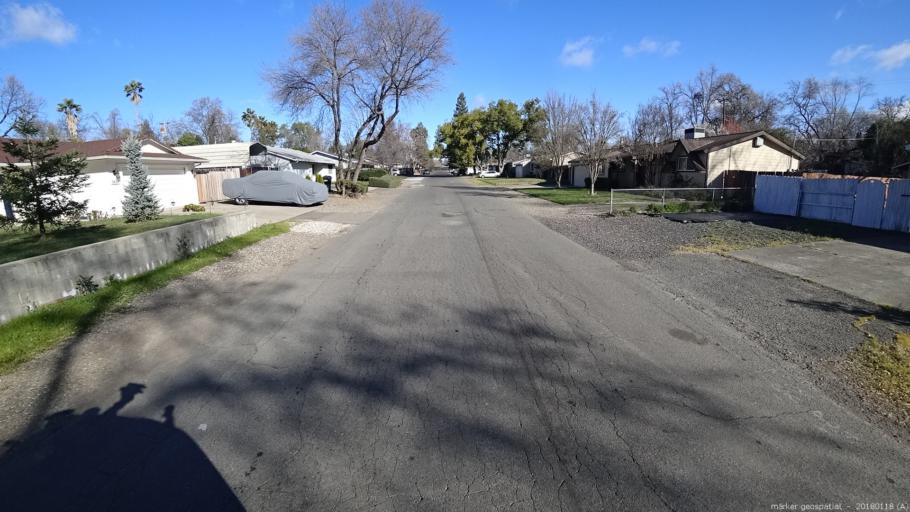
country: US
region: California
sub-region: Sacramento County
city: Orangevale
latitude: 38.6691
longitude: -121.2308
